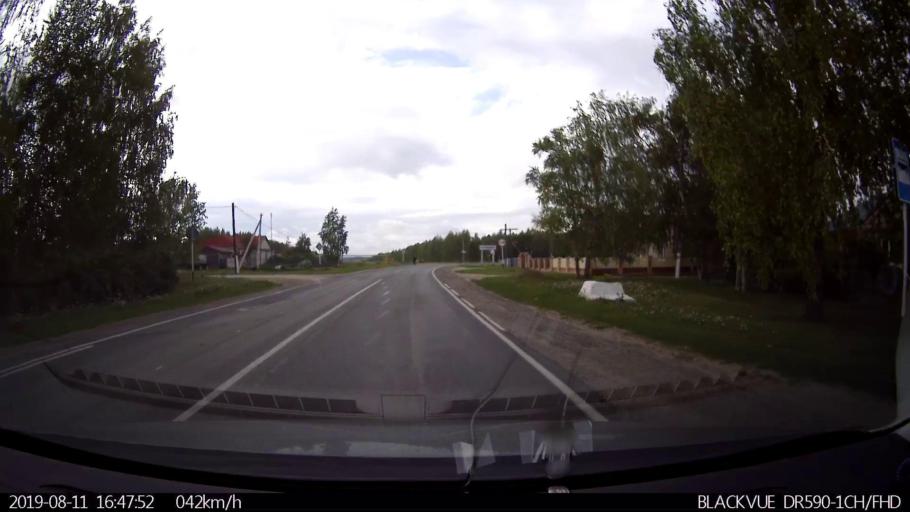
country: RU
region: Ulyanovsk
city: Mayna
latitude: 54.2052
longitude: 47.6926
